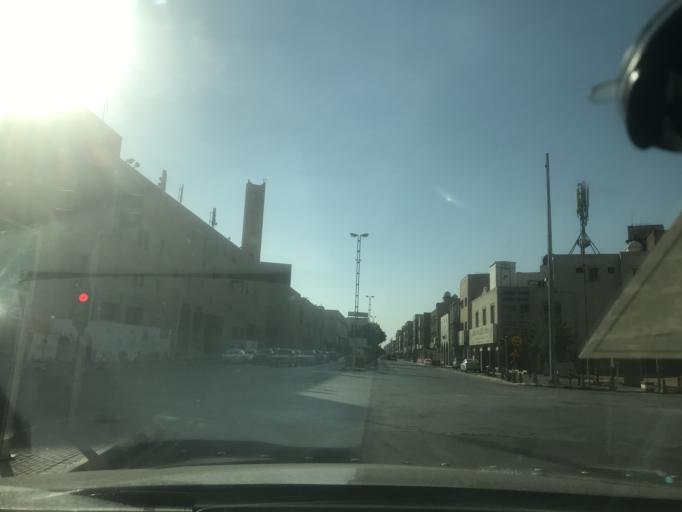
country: SA
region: Ar Riyad
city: Riyadh
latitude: 24.6319
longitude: 46.7121
